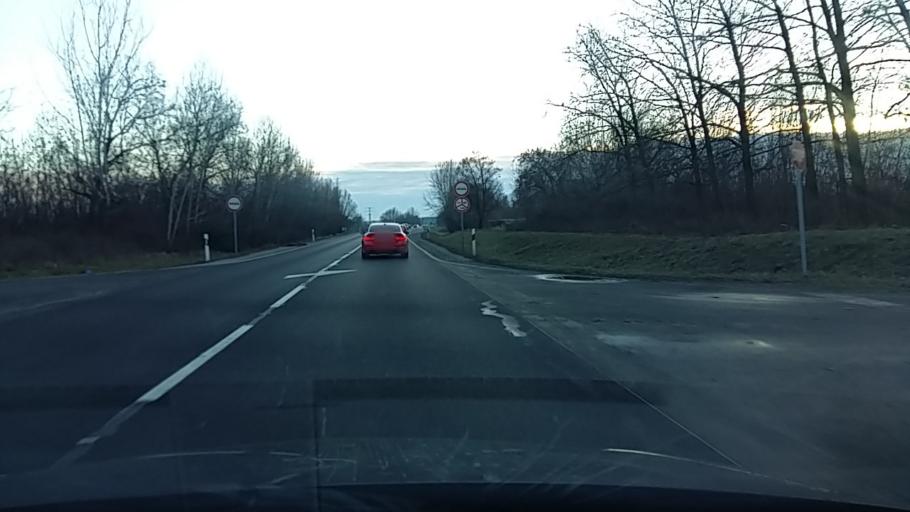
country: HU
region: Hajdu-Bihar
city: Hajduhadhaz
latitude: 47.6921
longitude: 21.6553
